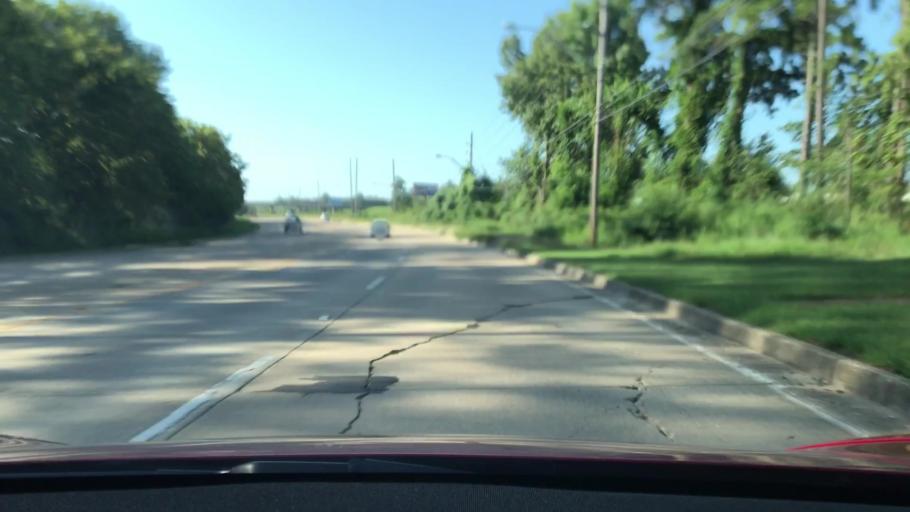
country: US
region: Louisiana
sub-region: Bossier Parish
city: Bossier City
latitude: 32.4062
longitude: -93.7385
